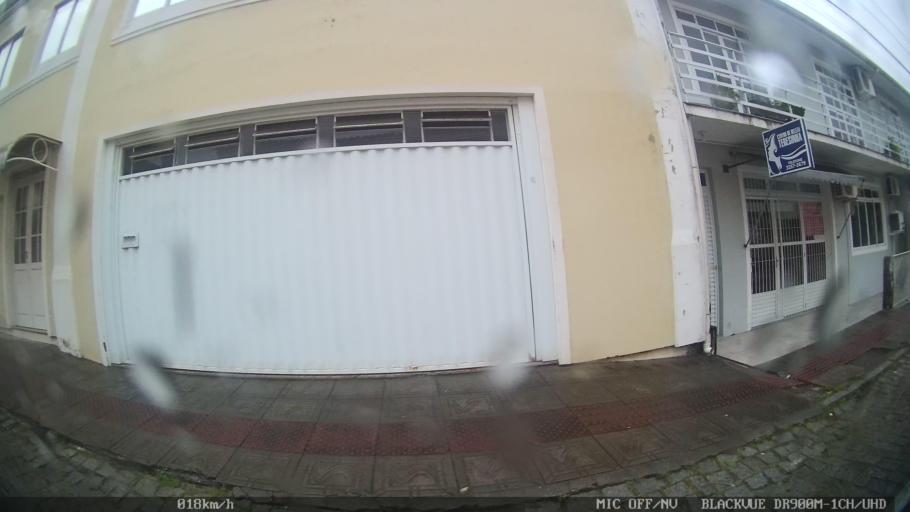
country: BR
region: Santa Catarina
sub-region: Sao Jose
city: Campinas
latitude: -27.6162
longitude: -48.6282
